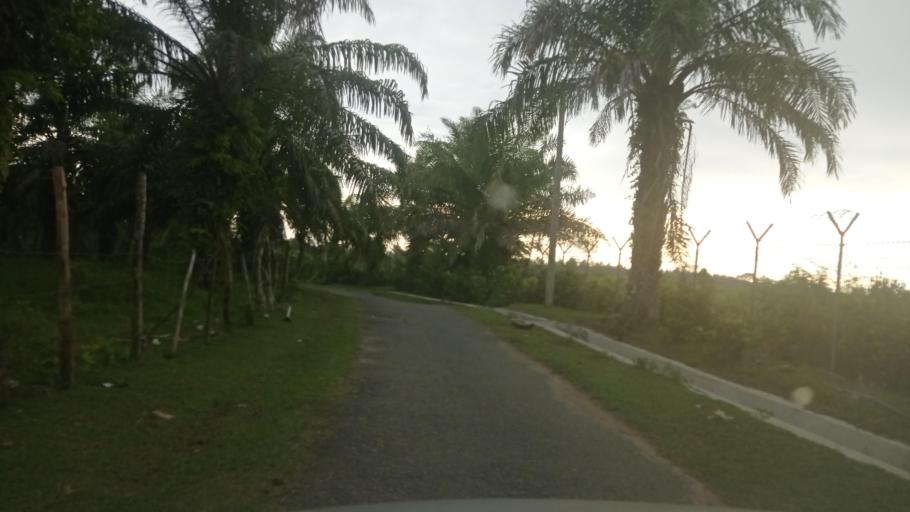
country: ID
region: Jambi
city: Sungai Penuh
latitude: -2.5475
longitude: 101.0896
